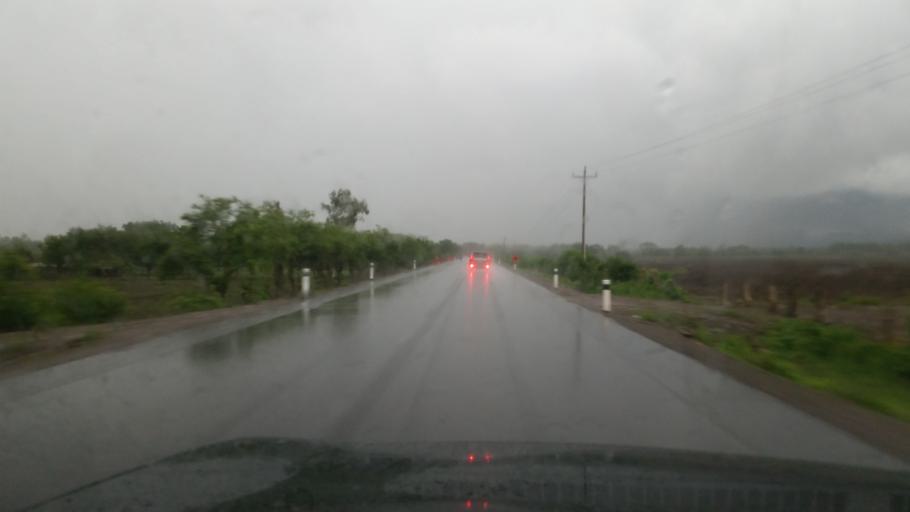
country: NI
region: Chinandega
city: Chichigalpa
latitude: 12.7723
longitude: -86.9185
